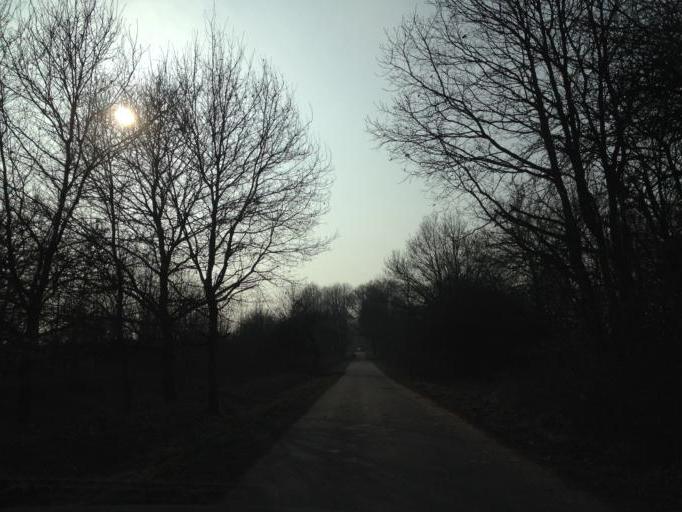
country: DE
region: Saarland
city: Mainzweiler
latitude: 49.4307
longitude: 7.1462
